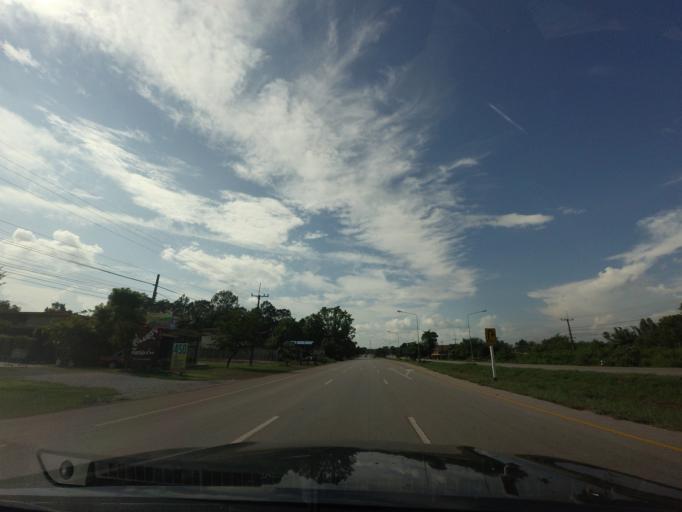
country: TH
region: Nong Khai
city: Sa Khrai
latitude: 17.6767
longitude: 102.7879
